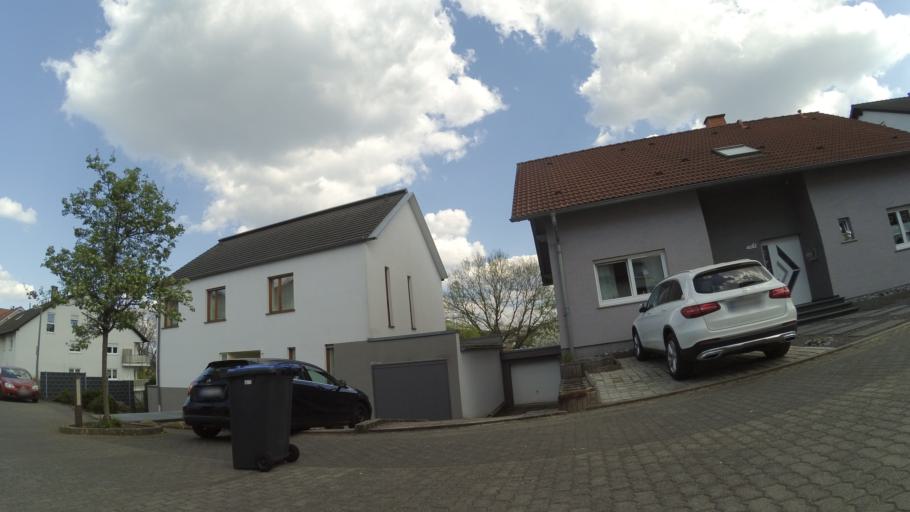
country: DE
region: Saarland
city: Riegelsberg
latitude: 49.3042
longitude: 6.9328
